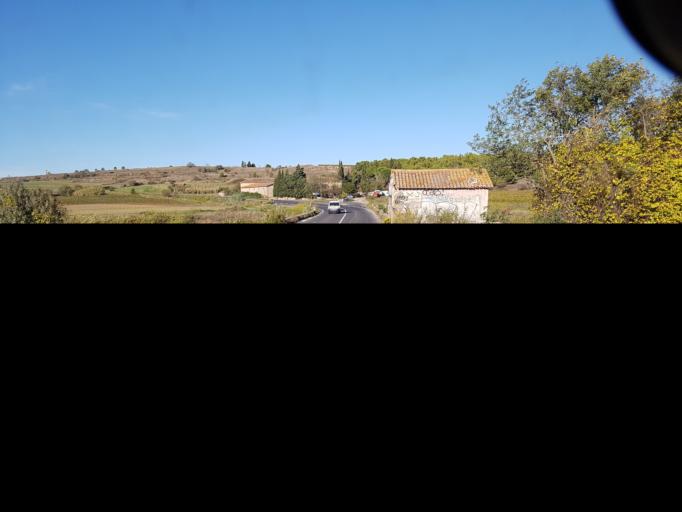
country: FR
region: Languedoc-Roussillon
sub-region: Departement de l'Aude
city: Coursan
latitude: 43.2652
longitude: 3.0804
